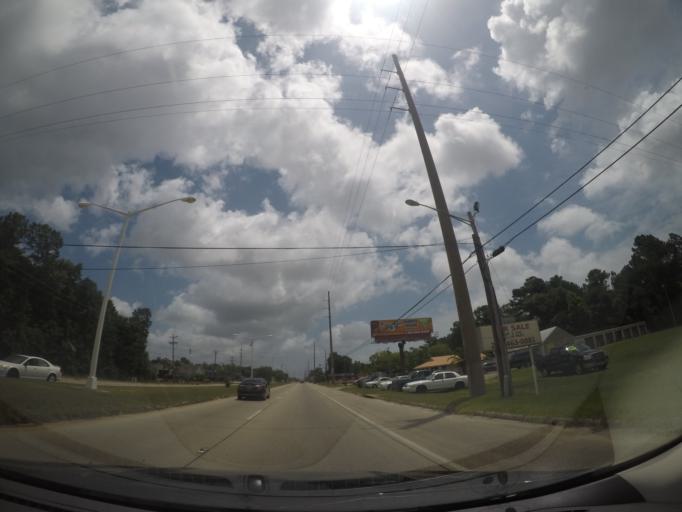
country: US
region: Mississippi
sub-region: Hancock County
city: Waveland
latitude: 30.3005
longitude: -89.3945
